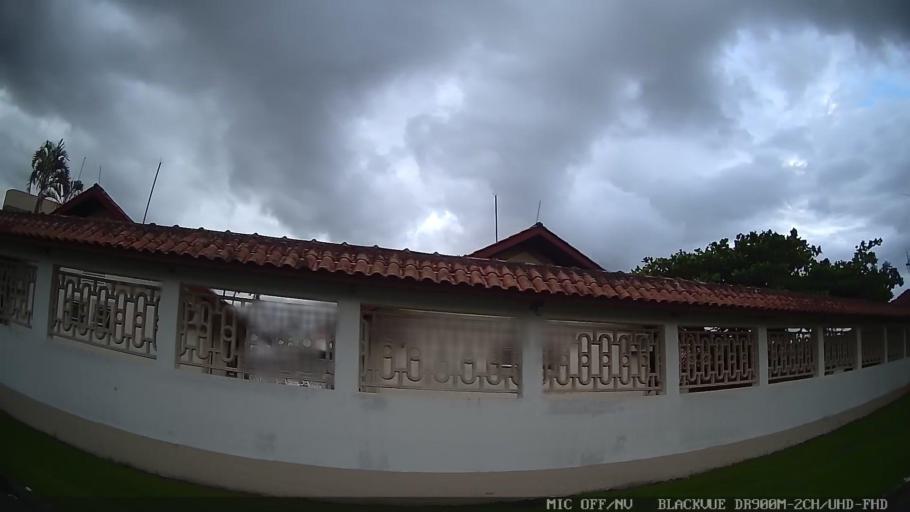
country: BR
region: Sao Paulo
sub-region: Sao Sebastiao
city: Sao Sebastiao
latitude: -23.6923
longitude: -45.4321
